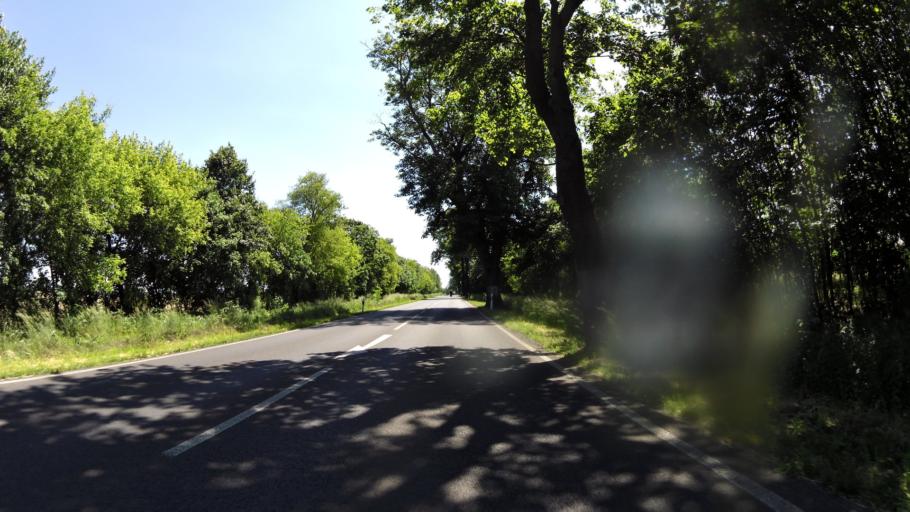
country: DE
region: Brandenburg
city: Frankfurt (Oder)
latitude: 52.3769
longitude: 14.5212
